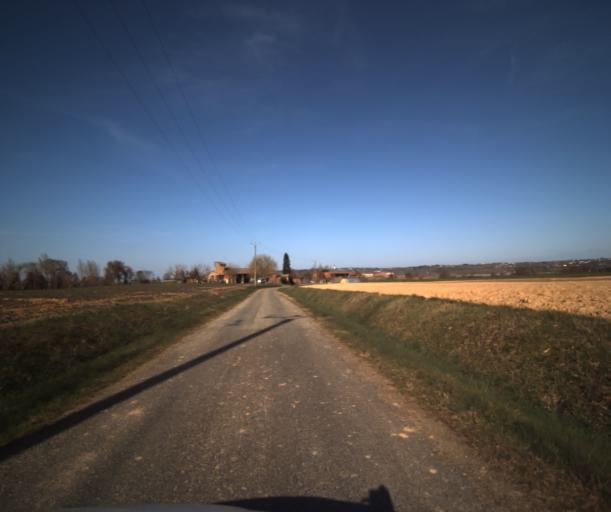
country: FR
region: Midi-Pyrenees
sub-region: Departement du Tarn-et-Garonne
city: Corbarieu
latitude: 43.9344
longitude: 1.3377
